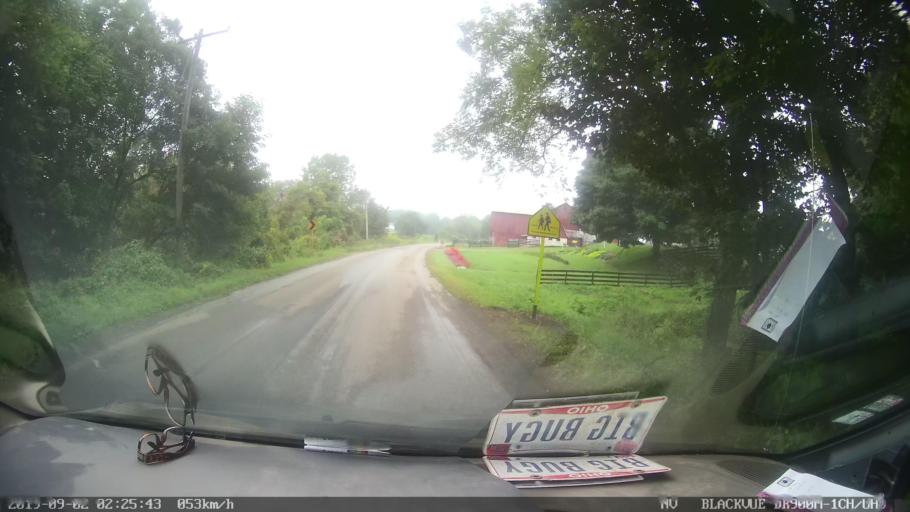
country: US
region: Ohio
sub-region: Knox County
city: Fredericktown
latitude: 40.5523
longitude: -82.6715
